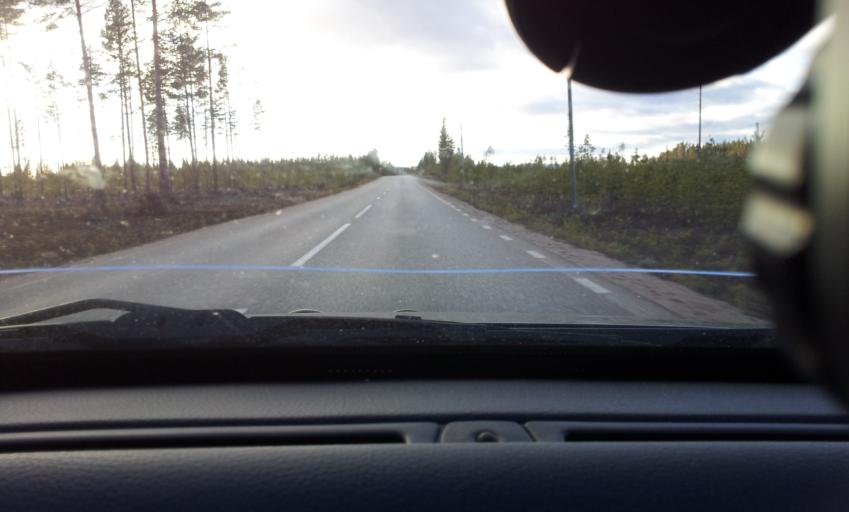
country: SE
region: Jaemtland
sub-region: Harjedalens Kommun
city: Sveg
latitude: 62.1263
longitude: 14.9824
